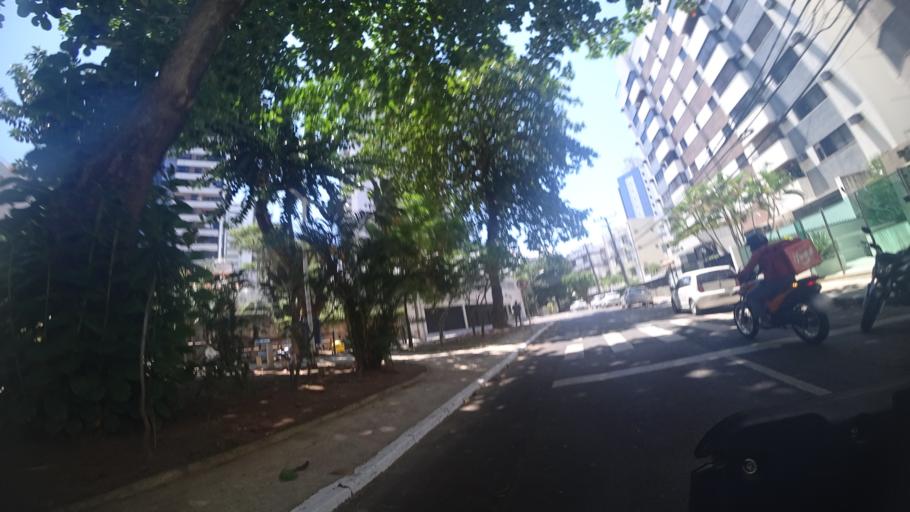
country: BR
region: Bahia
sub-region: Salvador
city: Salvador
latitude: -12.9872
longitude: -38.4590
